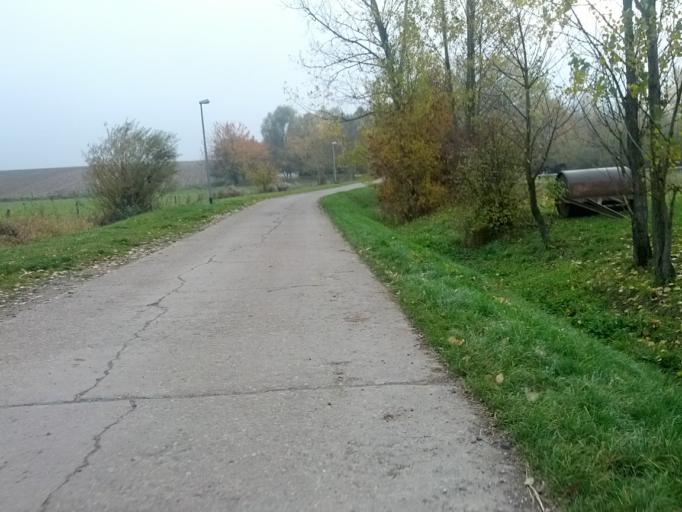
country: DE
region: Thuringia
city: Bischofroda
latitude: 50.9900
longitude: 10.4064
